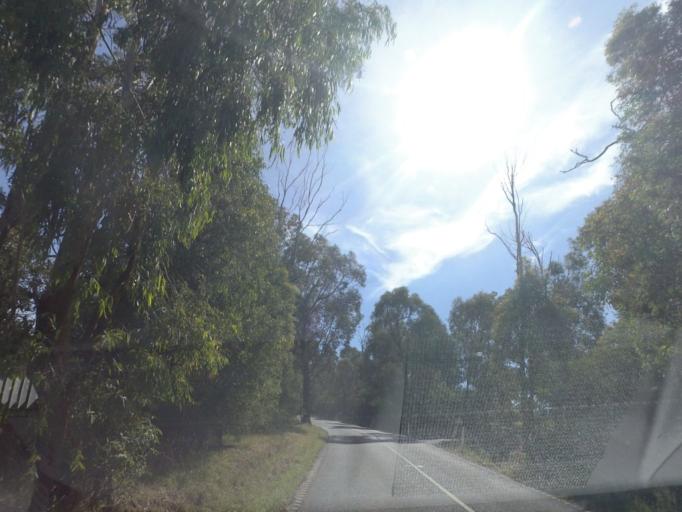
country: AU
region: Victoria
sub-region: Nillumbik
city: Saint Andrews
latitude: -37.5817
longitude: 145.2877
